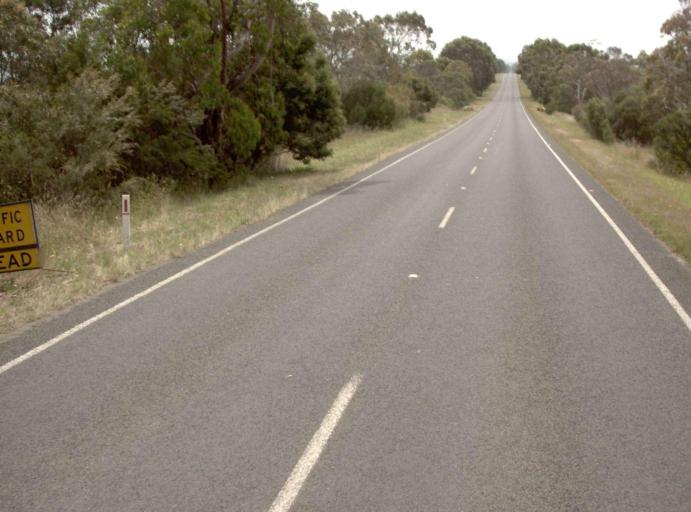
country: AU
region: Victoria
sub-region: Latrobe
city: Traralgon
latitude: -38.5036
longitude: 146.7105
